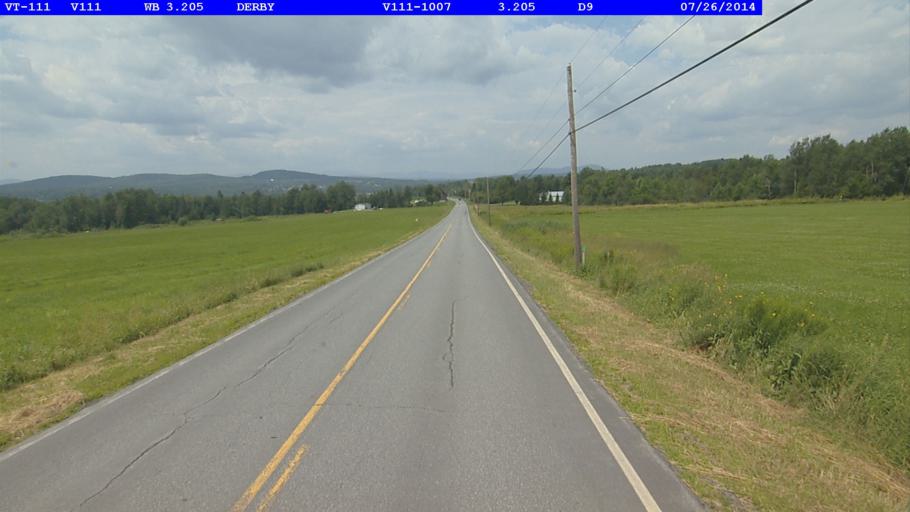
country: US
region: Vermont
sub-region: Orleans County
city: Newport
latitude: 44.9354
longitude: -72.0761
